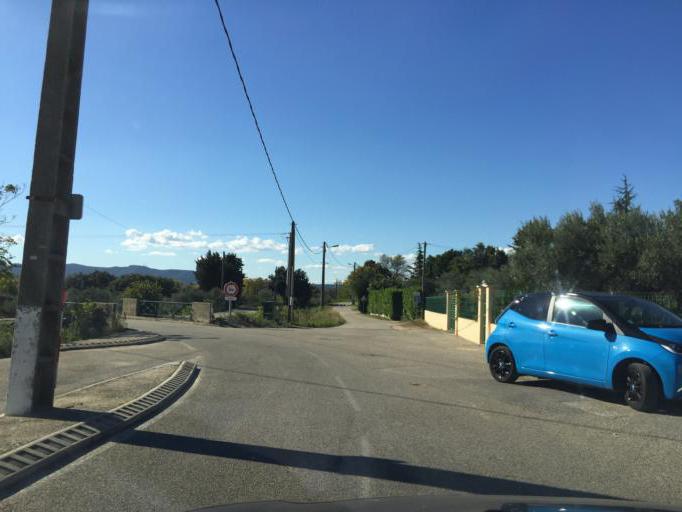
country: FR
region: Provence-Alpes-Cote d'Azur
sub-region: Departement du Vaucluse
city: Mornas
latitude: 44.1990
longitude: 4.7383
